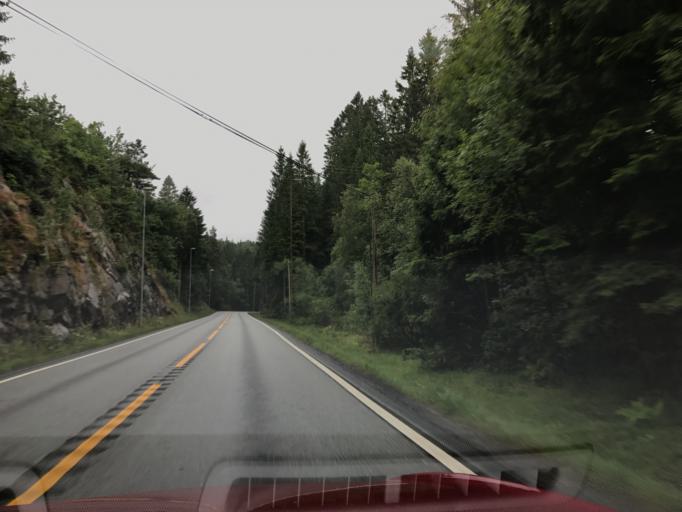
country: NO
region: Vest-Agder
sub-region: Mandal
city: Mandal
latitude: 58.0535
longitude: 7.5659
